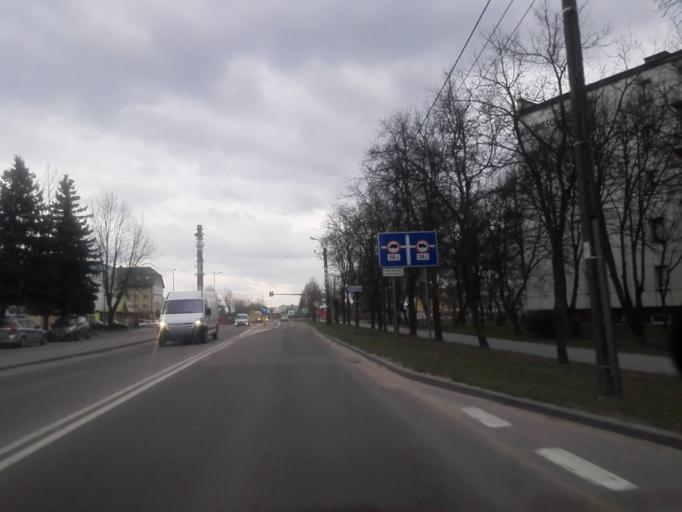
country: PL
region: Podlasie
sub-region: Powiat augustowski
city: Augustow
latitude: 53.8385
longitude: 22.9888
